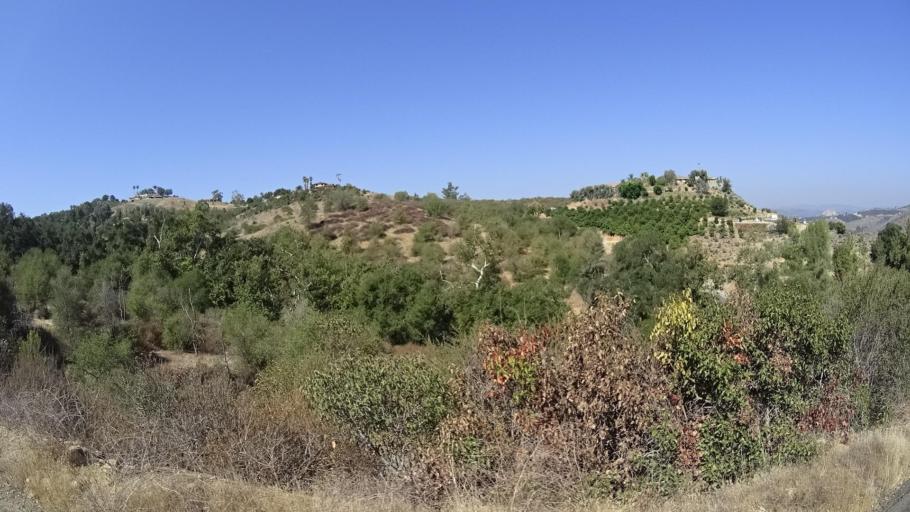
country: US
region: California
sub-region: San Diego County
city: Rainbow
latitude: 33.4065
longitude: -117.2031
